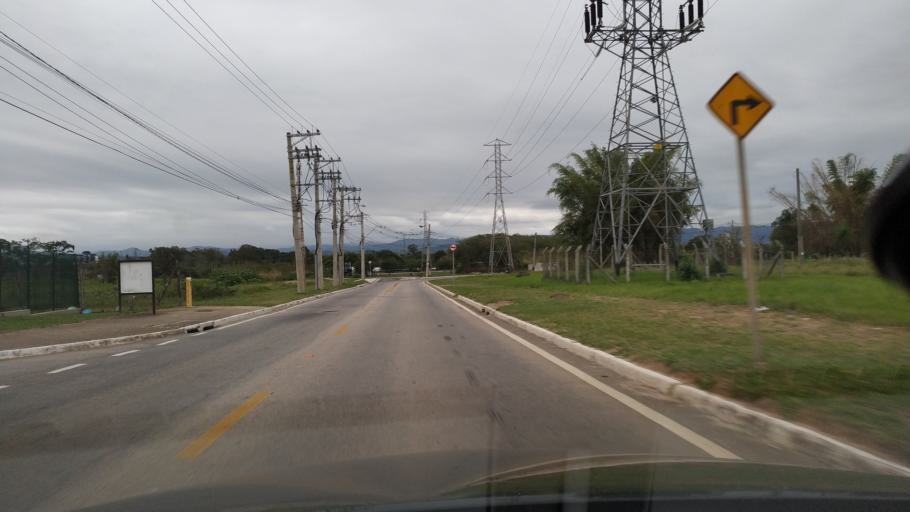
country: BR
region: Sao Paulo
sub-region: Cacapava
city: Cacapava
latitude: -23.1556
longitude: -45.7857
